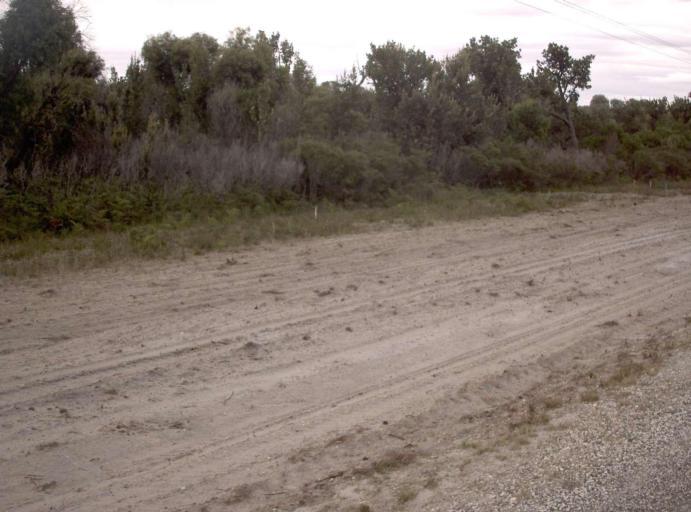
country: AU
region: Victoria
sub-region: East Gippsland
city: Bairnsdale
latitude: -38.0978
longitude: 147.5090
